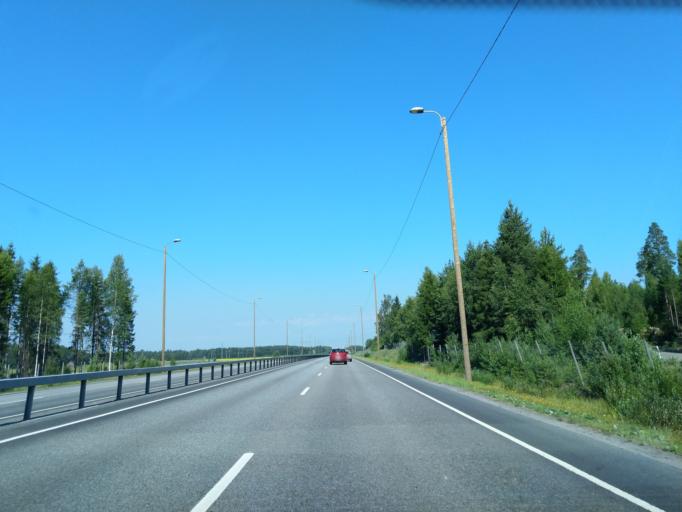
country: FI
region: Satakunta
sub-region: Pori
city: Nakkila
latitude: 61.3354
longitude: 22.0503
